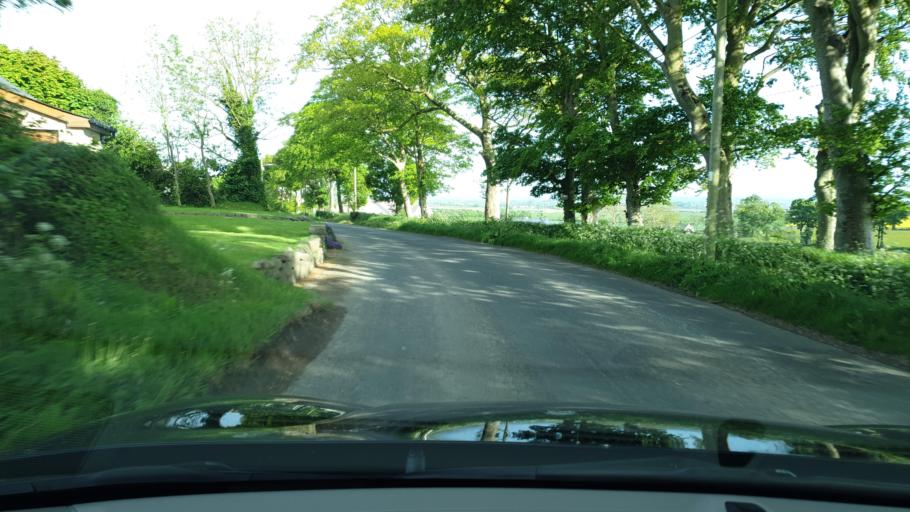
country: IE
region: Leinster
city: Balrothery
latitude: 53.5610
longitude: -6.1809
